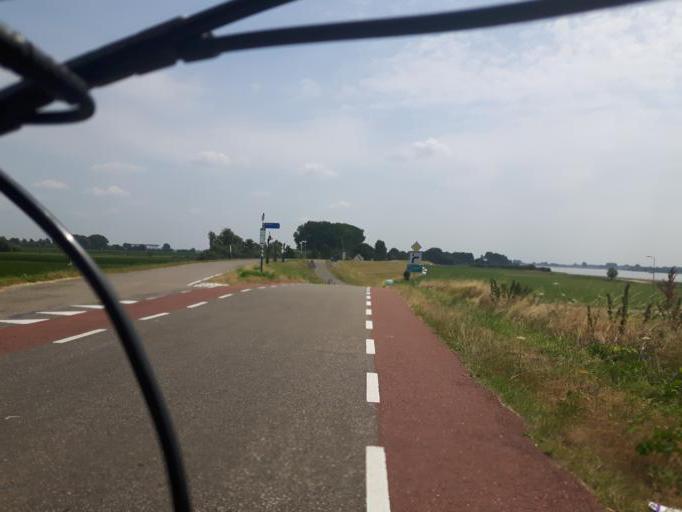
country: NL
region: South Holland
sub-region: Gemeente Leerdam
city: Leerdam
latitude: 51.8301
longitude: 5.0927
